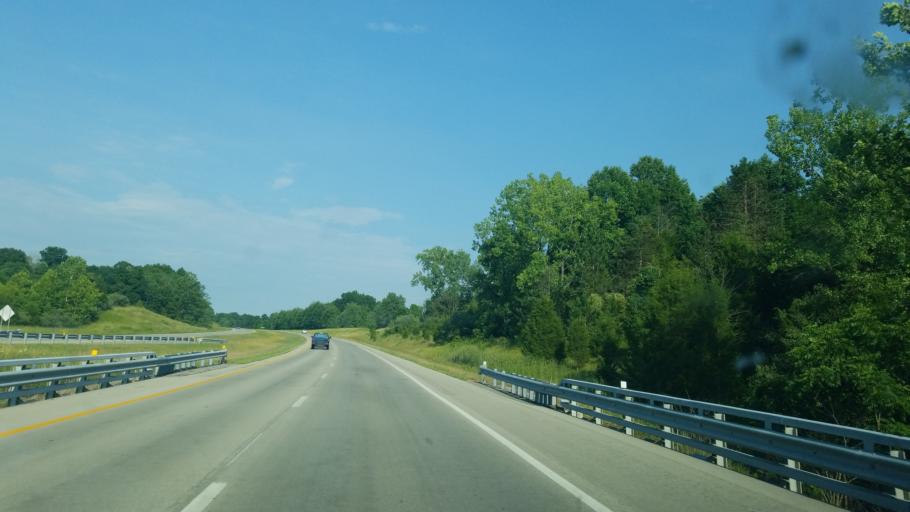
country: US
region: Ohio
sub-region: Brown County
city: Mount Orab
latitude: 39.0196
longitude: -83.8605
